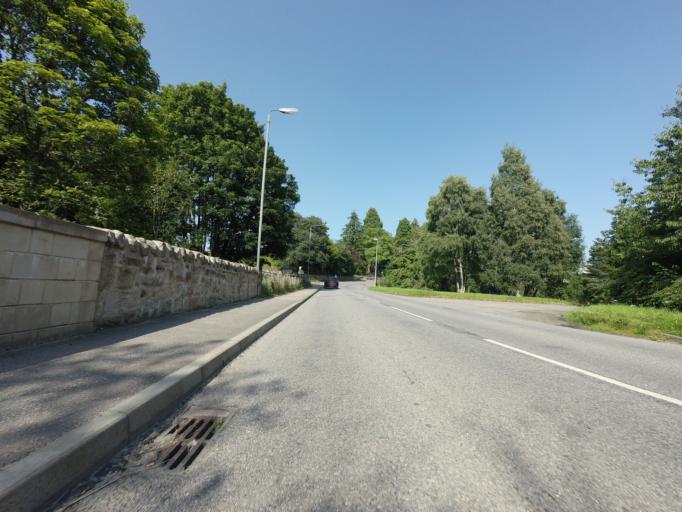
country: GB
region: Scotland
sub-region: Highland
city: Evanton
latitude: 57.6656
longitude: -4.3342
